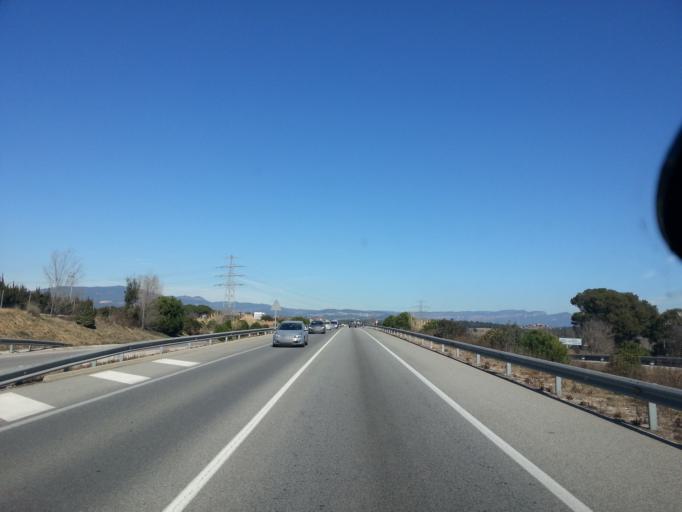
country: ES
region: Catalonia
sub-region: Provincia de Barcelona
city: Santa Perpetua de Mogoda
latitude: 41.5670
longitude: 2.1880
